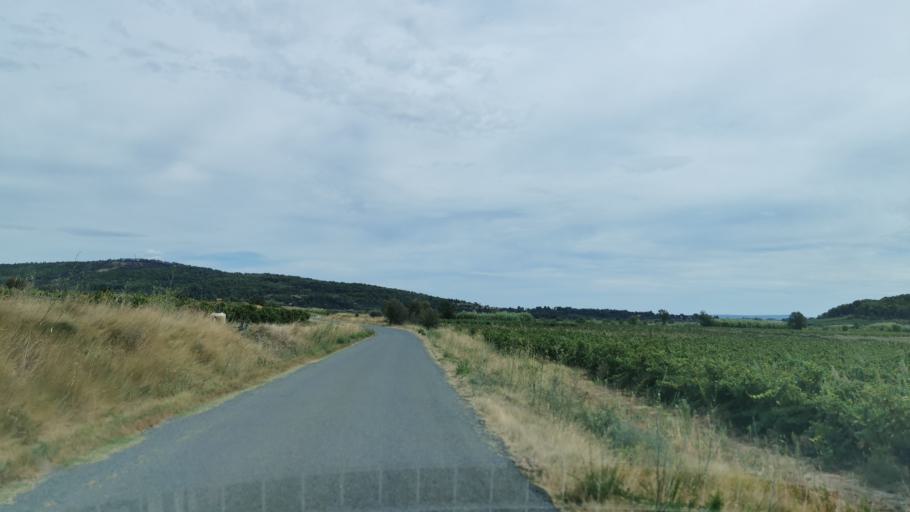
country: FR
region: Languedoc-Roussillon
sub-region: Departement de l'Aude
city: Bize-Minervois
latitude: 43.3097
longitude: 2.8496
